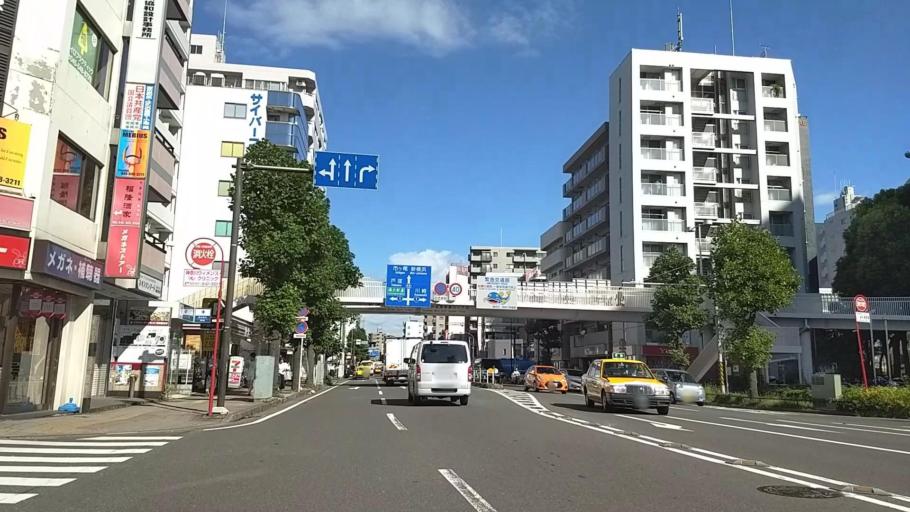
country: JP
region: Kanagawa
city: Yokohama
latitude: 35.4793
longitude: 139.6325
